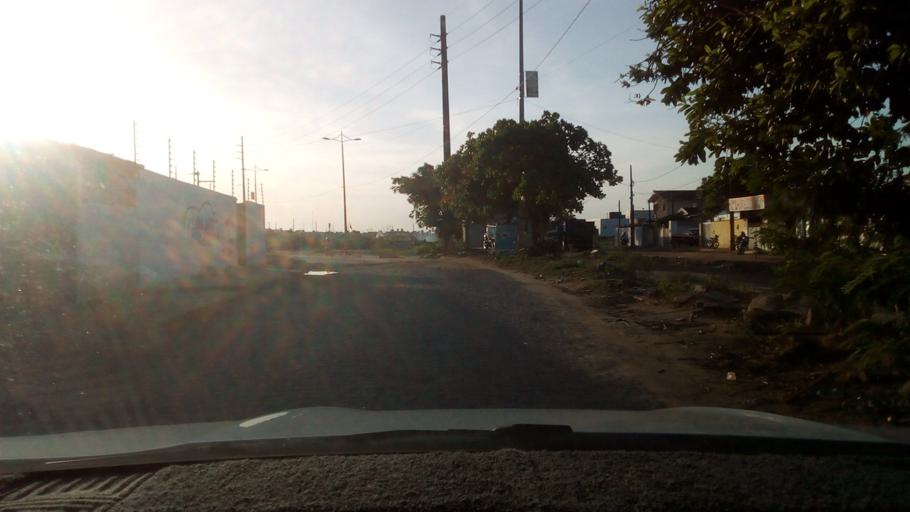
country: BR
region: Paraiba
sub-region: Conde
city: Conde
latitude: -7.1992
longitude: -34.8651
